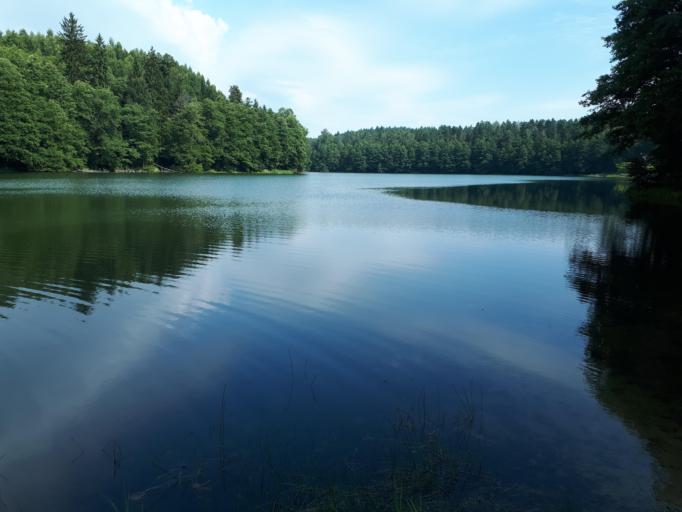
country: LT
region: Vilnius County
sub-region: Trakai
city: Rudiskes
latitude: 54.5302
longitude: 24.7016
